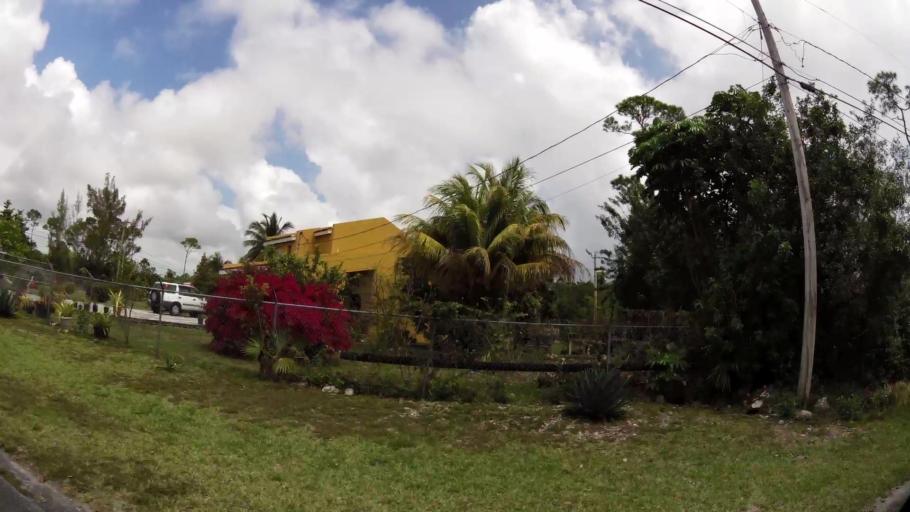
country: BS
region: Freeport
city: Lucaya
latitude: 26.5236
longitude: -78.6520
